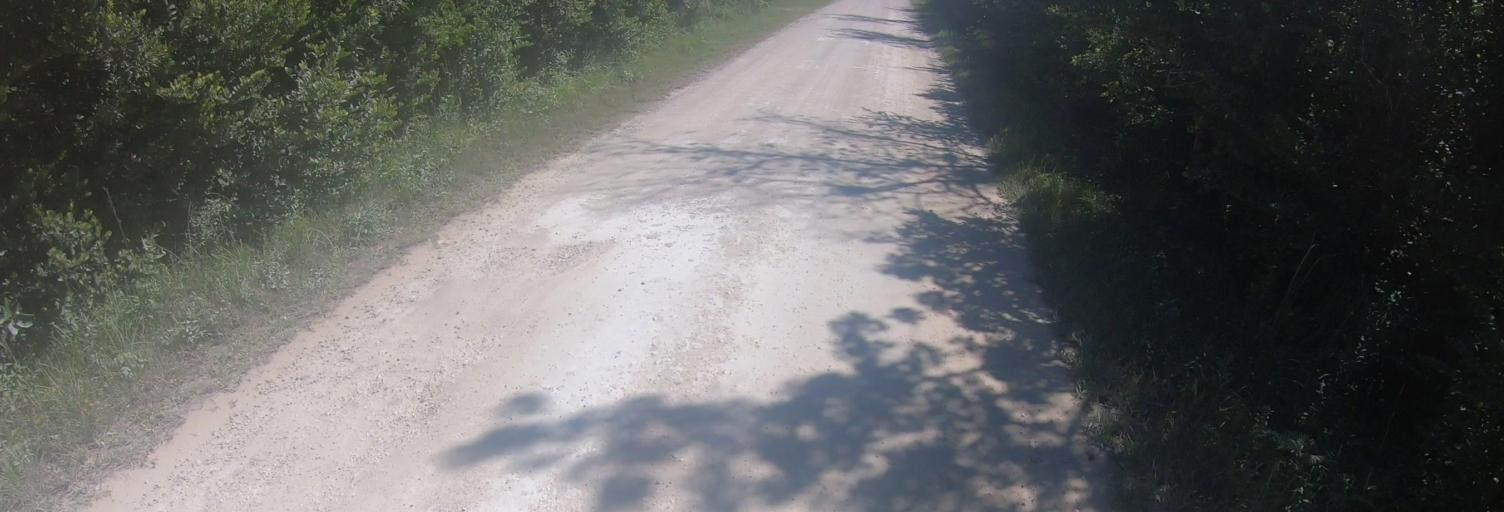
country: US
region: Florida
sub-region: Miami-Dade County
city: The Hammocks
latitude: 25.7543
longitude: -80.9778
